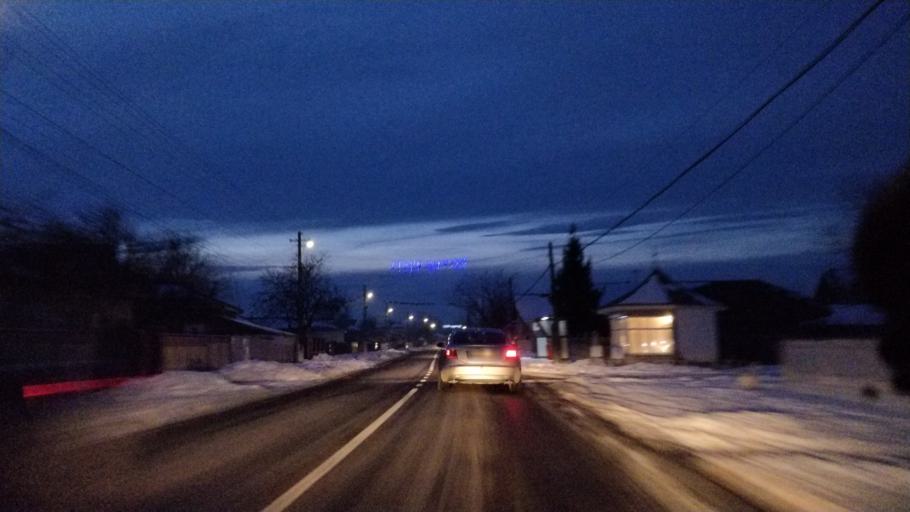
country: RO
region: Vrancea
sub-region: Comuna Rastoaca
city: Rastoaca
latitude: 45.6568
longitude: 27.2922
